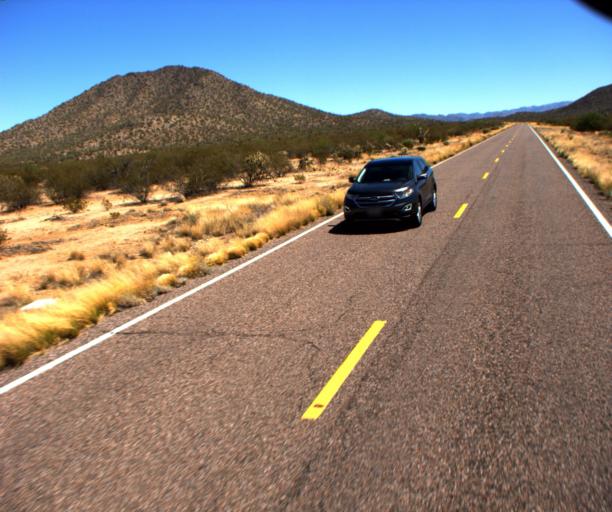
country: US
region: Arizona
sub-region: Yavapai County
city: Congress
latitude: 34.0896
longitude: -113.0090
